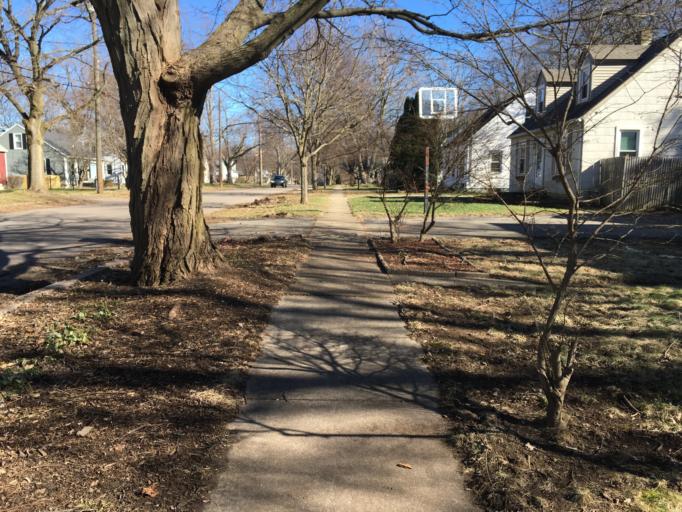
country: US
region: Michigan
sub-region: Kalamazoo County
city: Westwood
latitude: 42.2628
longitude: -85.6259
